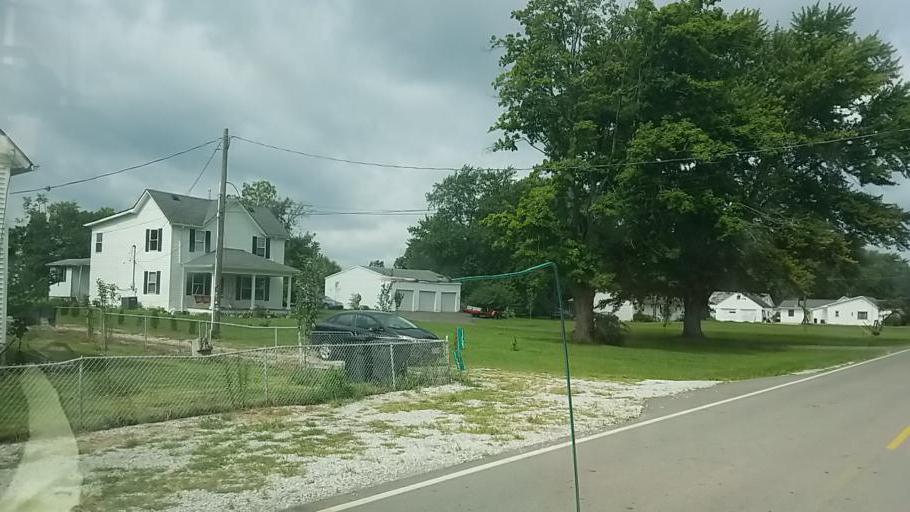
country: US
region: Ohio
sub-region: Madison County
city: Mount Sterling
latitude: 39.7716
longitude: -83.2092
